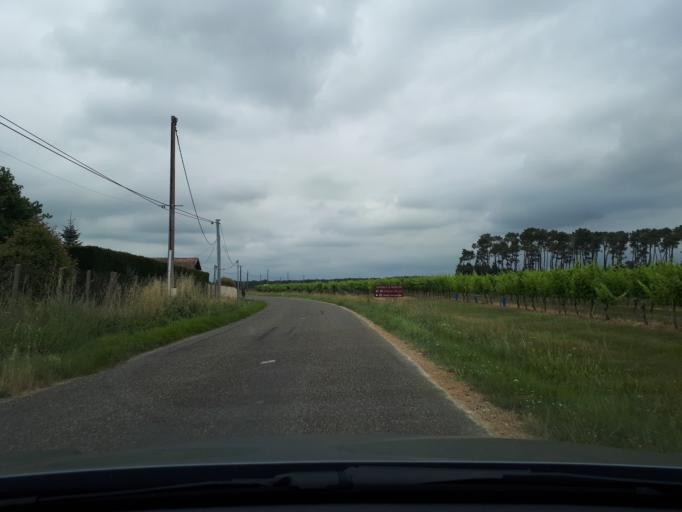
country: FR
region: Midi-Pyrenees
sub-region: Departement du Tarn-et-Garonne
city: Campsas
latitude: 43.8819
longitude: 1.3372
